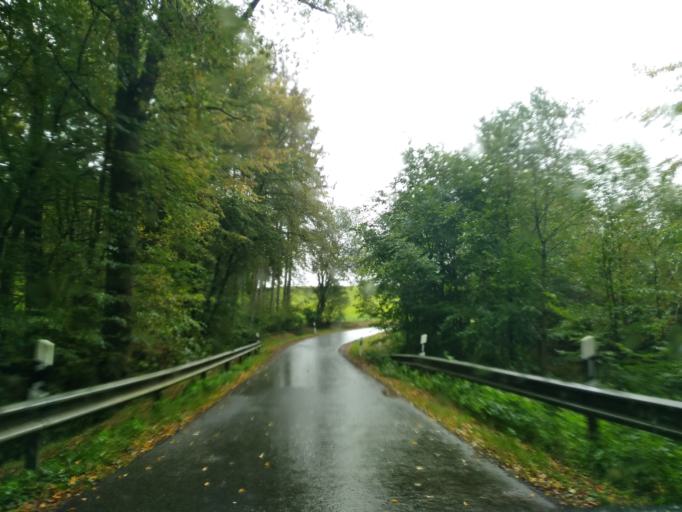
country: DE
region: Rheinland-Pfalz
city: Kescheid
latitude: 50.6707
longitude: 7.4526
